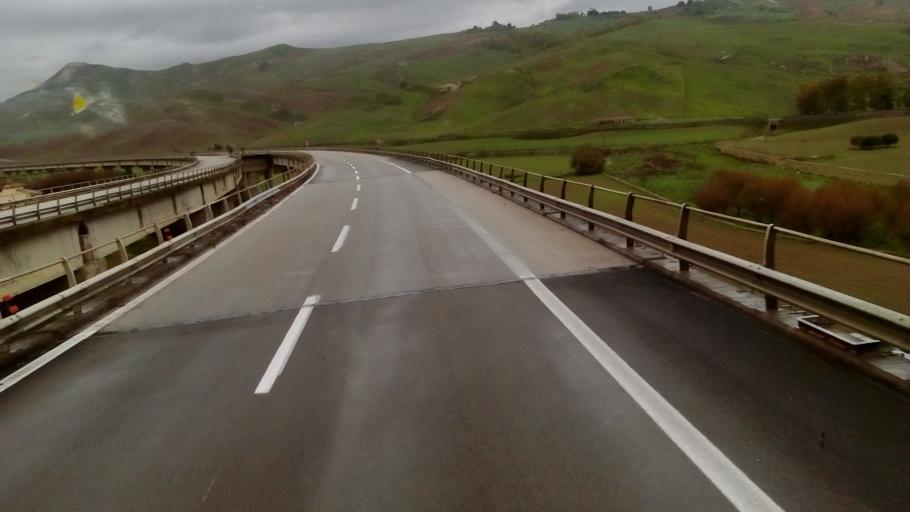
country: IT
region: Sicily
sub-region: Enna
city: Villarosa
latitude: 37.5622
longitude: 14.2002
